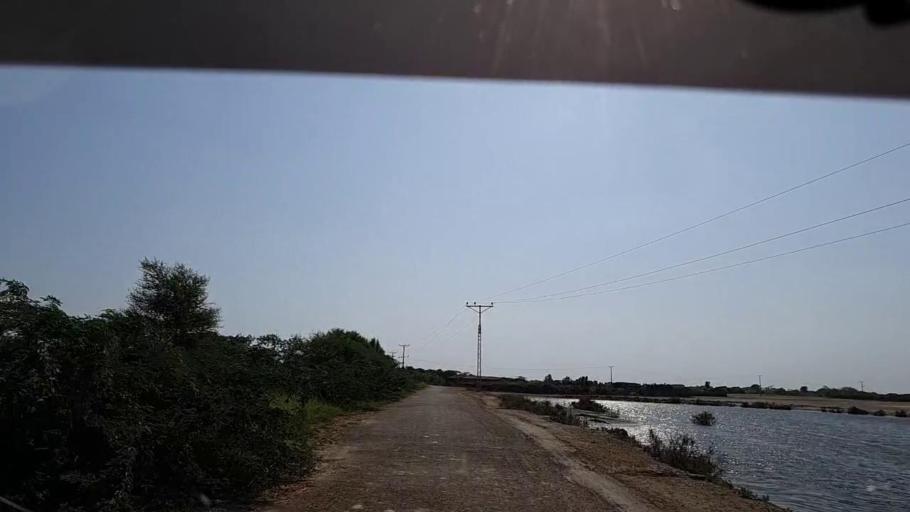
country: PK
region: Sindh
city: Badin
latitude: 24.6324
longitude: 68.7843
